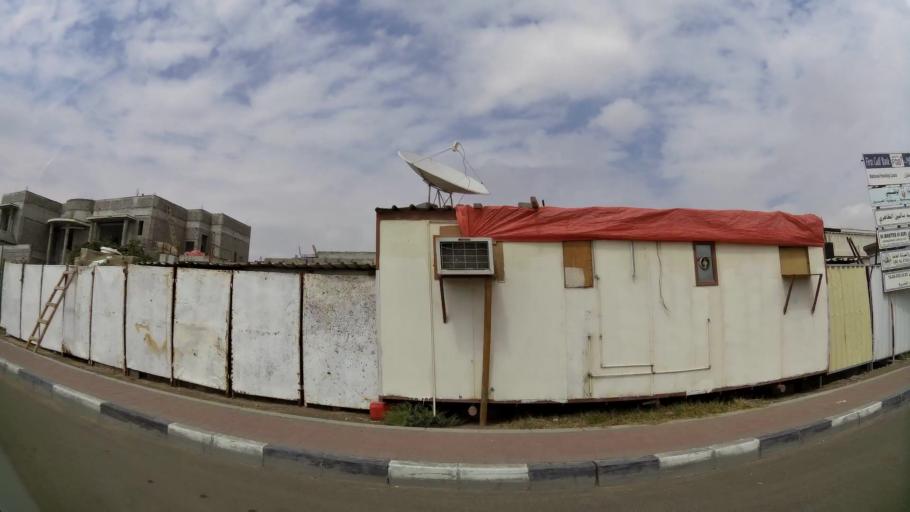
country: AE
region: Abu Dhabi
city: Al Ain
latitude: 24.1994
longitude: 55.8023
